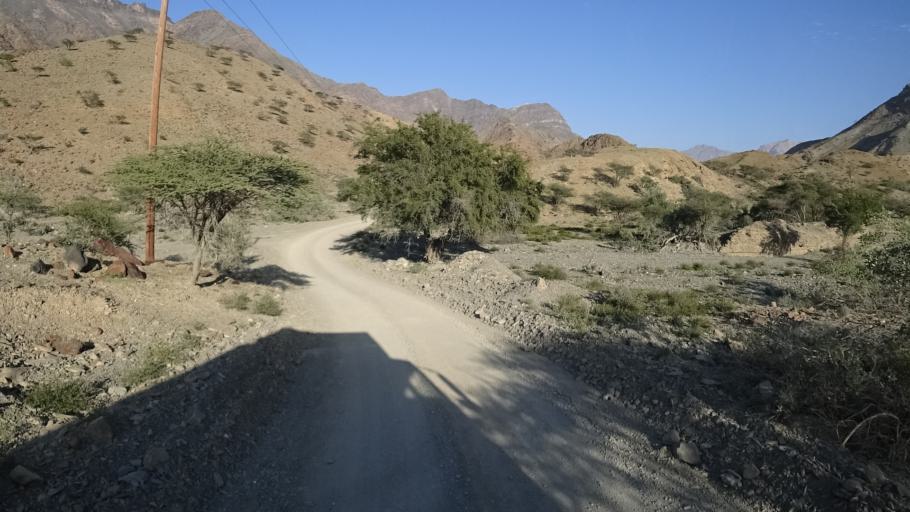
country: OM
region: Al Batinah
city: Rustaq
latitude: 23.2756
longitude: 57.3661
